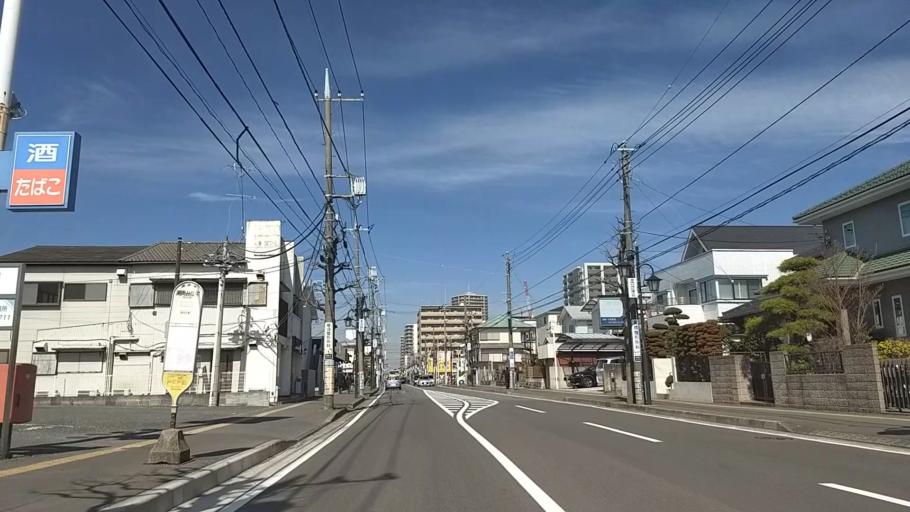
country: JP
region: Kanagawa
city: Fujisawa
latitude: 35.3924
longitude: 139.4640
